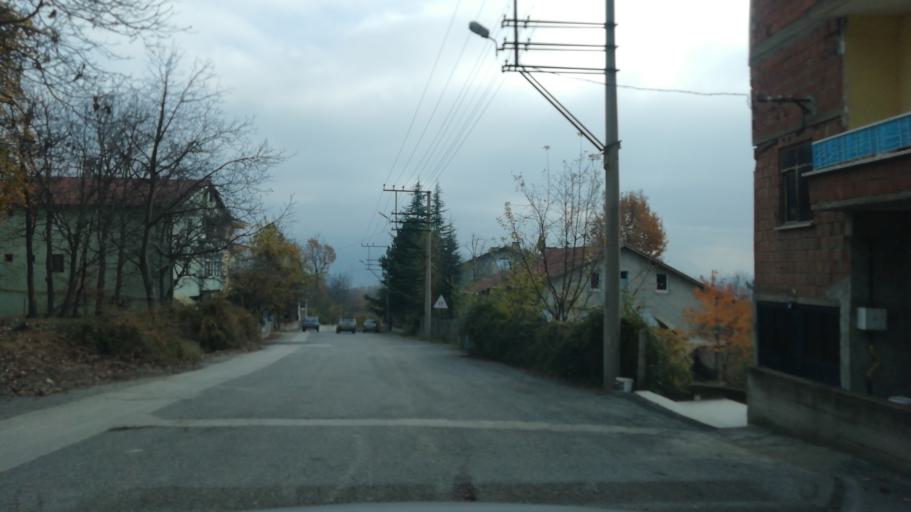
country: TR
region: Karabuk
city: Karabuk
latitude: 41.2263
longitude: 32.6220
